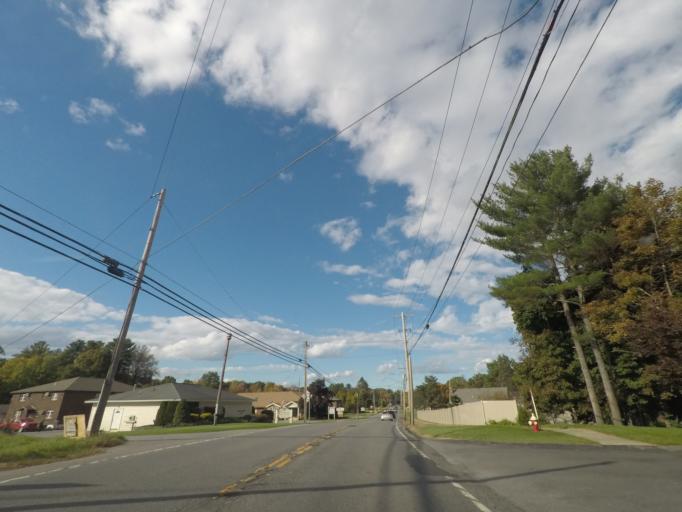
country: US
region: New York
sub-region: Schenectady County
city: Rotterdam
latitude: 42.7260
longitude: -73.9375
